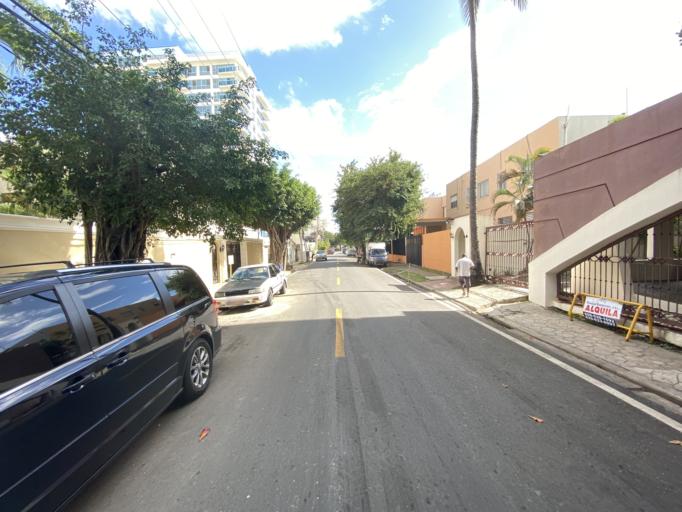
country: DO
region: Nacional
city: Ciudad Nueva
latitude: 18.4699
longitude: -69.9133
